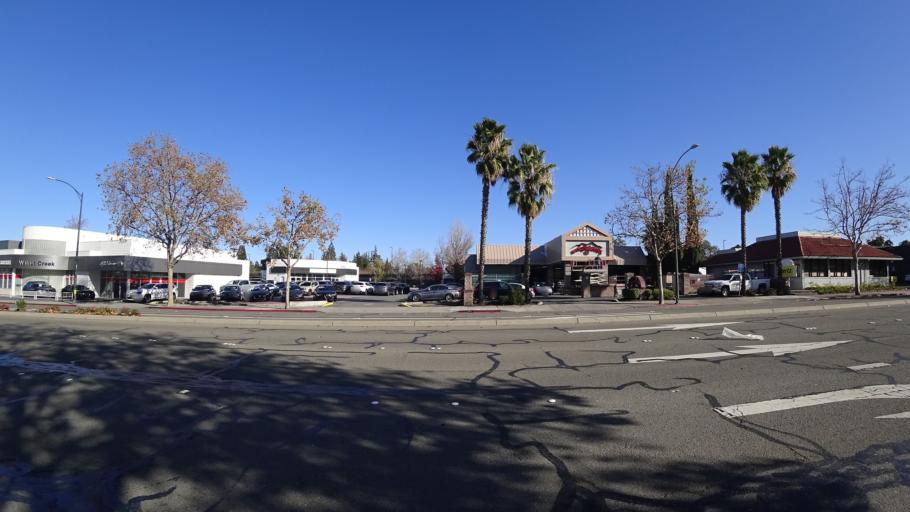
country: US
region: California
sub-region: Contra Costa County
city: Walnut Creek
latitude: 37.9113
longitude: -122.0655
